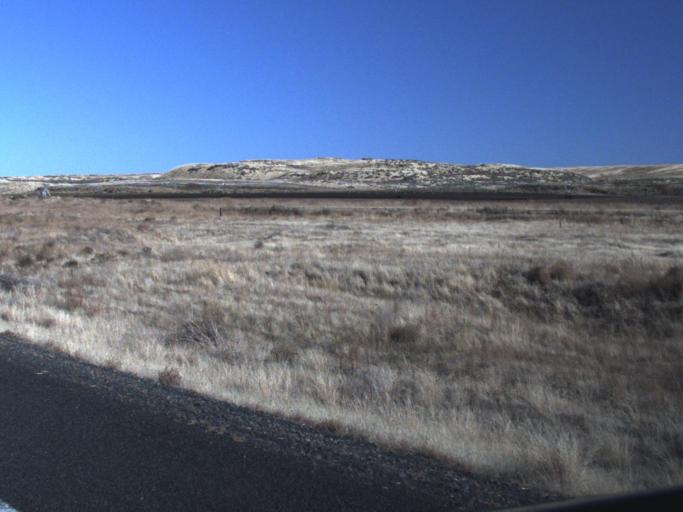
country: US
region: Washington
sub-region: Franklin County
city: Connell
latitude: 46.6682
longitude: -118.4753
